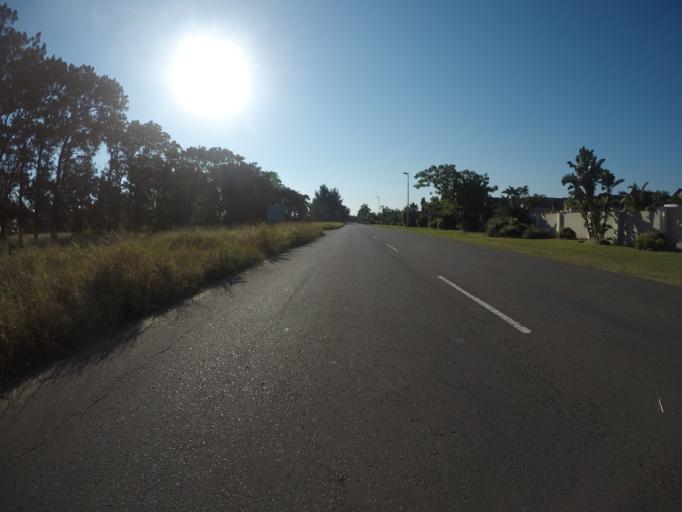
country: ZA
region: KwaZulu-Natal
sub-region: uThungulu District Municipality
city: Richards Bay
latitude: -28.7912
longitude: 32.0809
